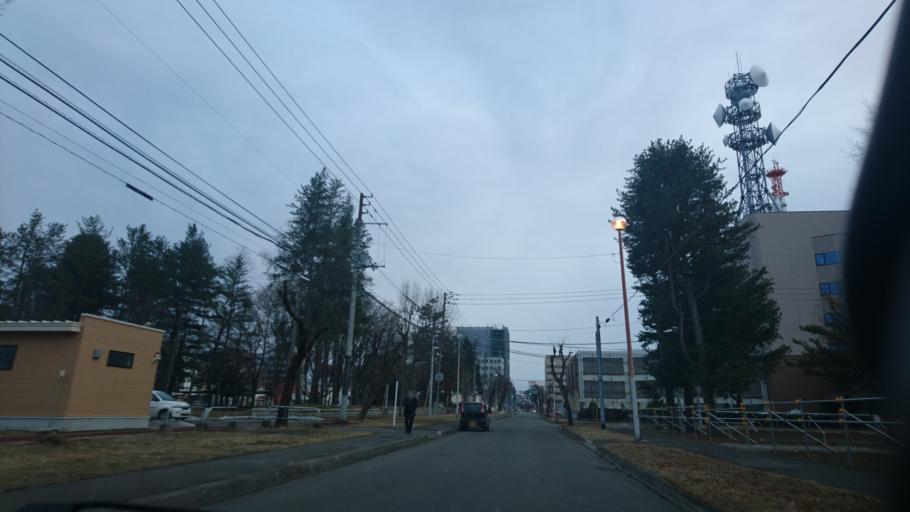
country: JP
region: Hokkaido
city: Obihiro
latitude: 42.9251
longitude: 143.1985
